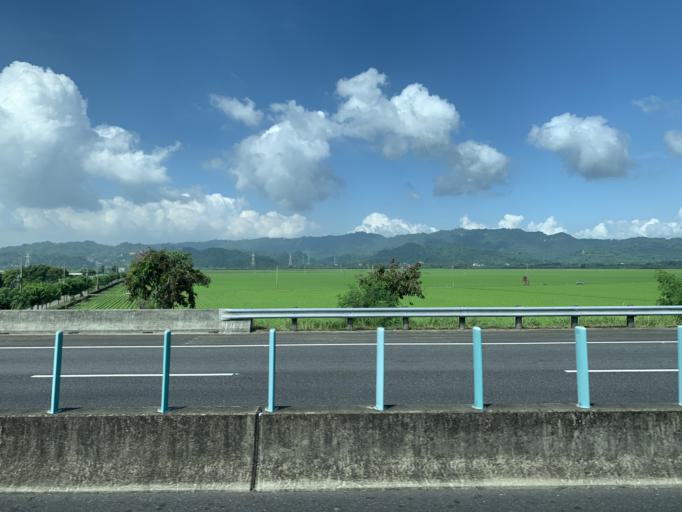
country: TW
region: Taiwan
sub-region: Pingtung
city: Pingtung
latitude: 22.8211
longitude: 120.4873
